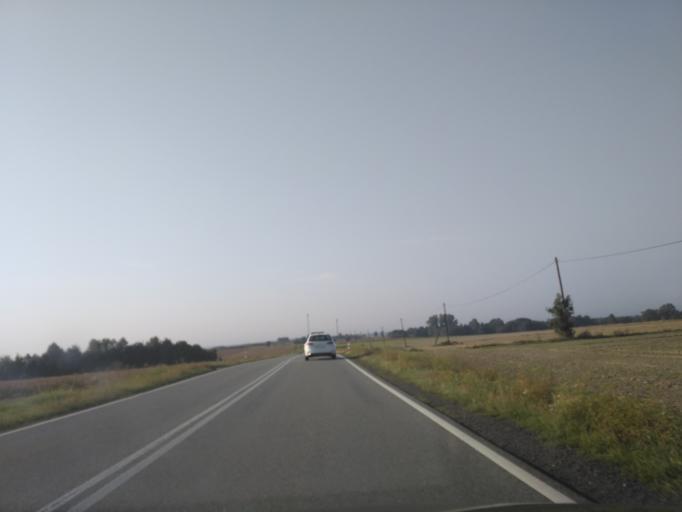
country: PL
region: Lublin Voivodeship
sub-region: Powiat janowski
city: Modliborzyce
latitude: 50.7783
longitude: 22.3240
